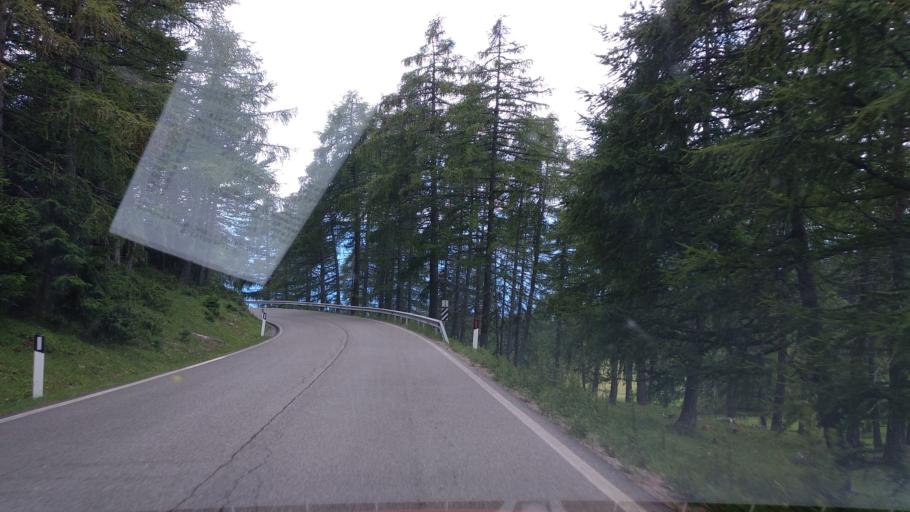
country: IT
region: Trentino-Alto Adige
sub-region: Bolzano
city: Avelengo
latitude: 46.6585
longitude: 11.2309
